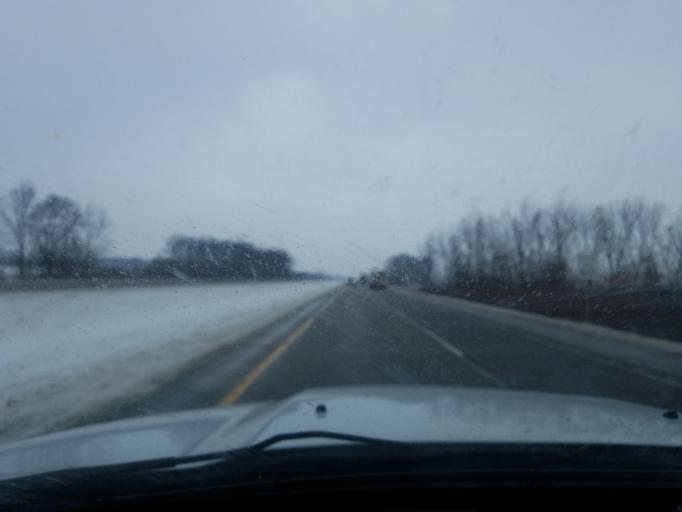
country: US
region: Indiana
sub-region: Marshall County
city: Argos
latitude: 41.1758
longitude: -86.2435
